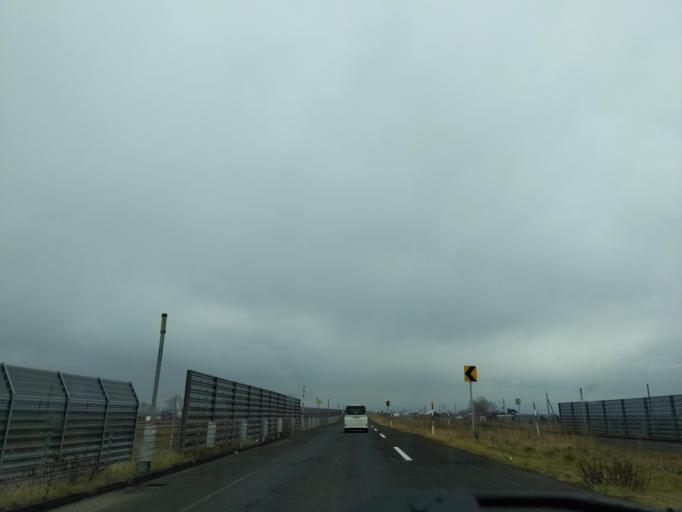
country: JP
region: Hokkaido
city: Tobetsu
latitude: 43.1849
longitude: 141.5338
